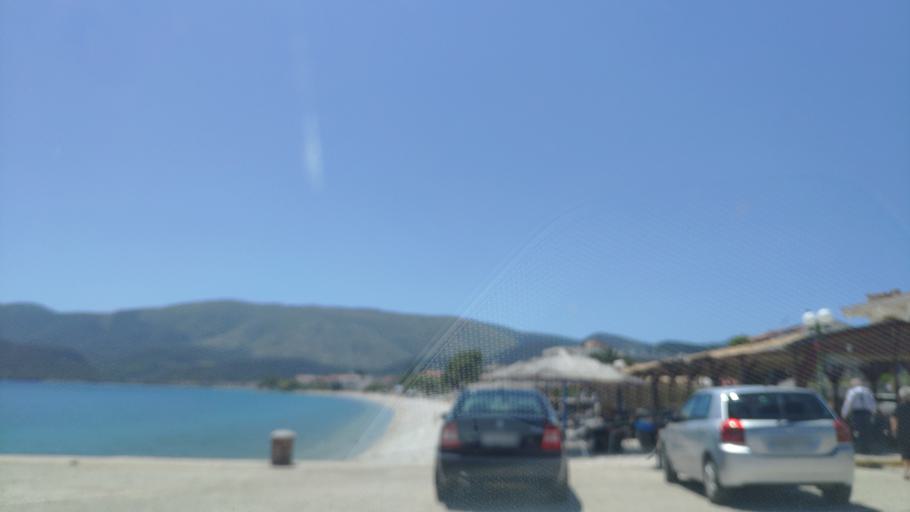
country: GR
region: Peloponnese
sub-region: Nomos Korinthias
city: Loutra Oraias Elenis
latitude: 37.8621
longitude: 22.9977
